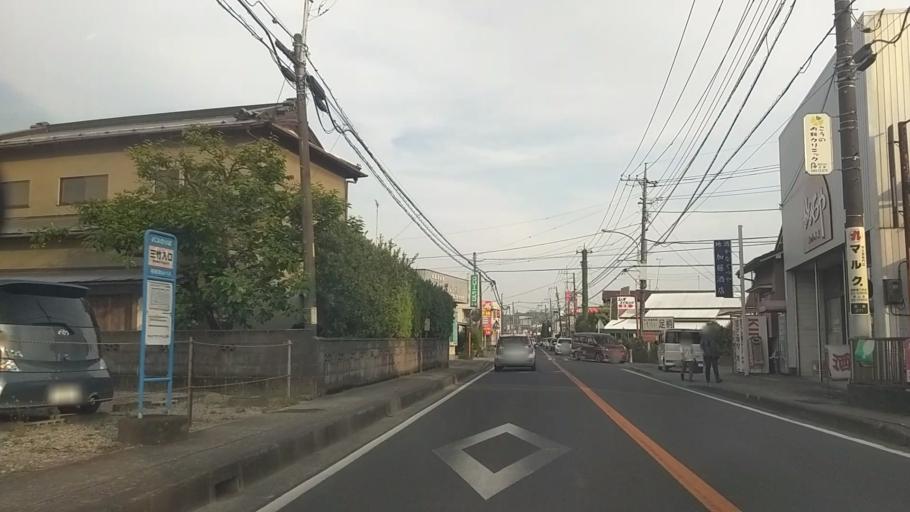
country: JP
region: Kanagawa
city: Odawara
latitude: 35.2948
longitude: 139.1315
